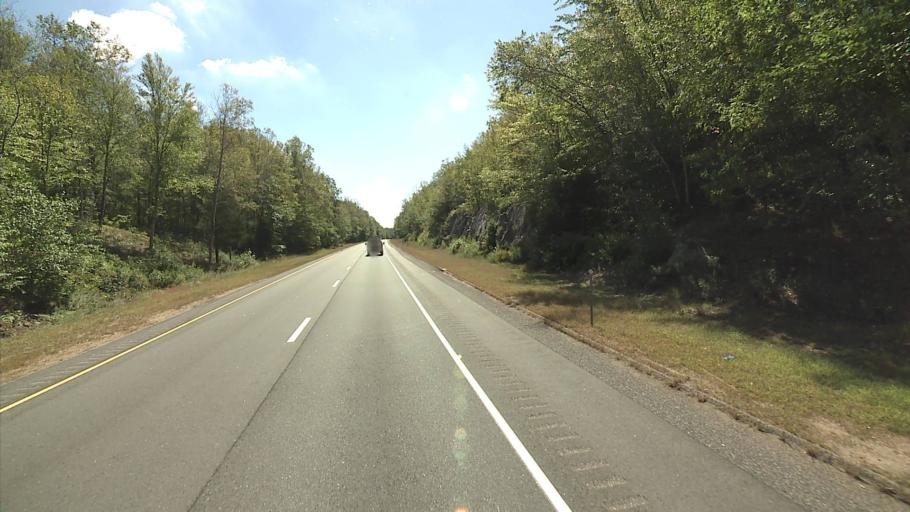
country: US
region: Connecticut
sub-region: New London County
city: Colchester
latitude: 41.5148
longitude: -72.3033
